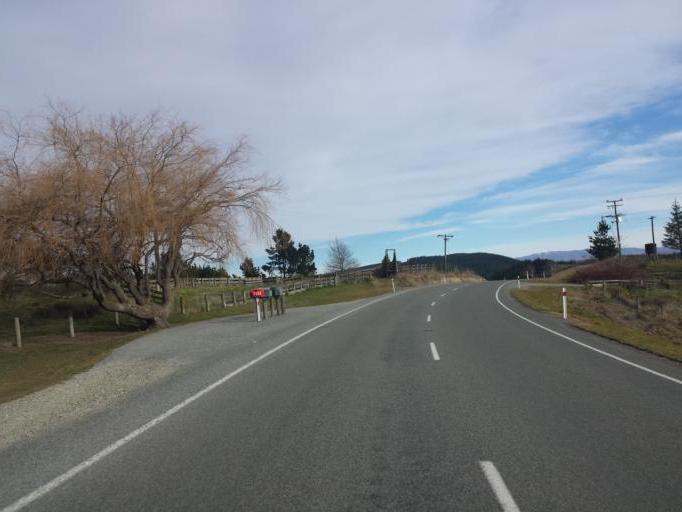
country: NZ
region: Canterbury
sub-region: Timaru District
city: Pleasant Point
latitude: -44.1229
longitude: 171.1089
